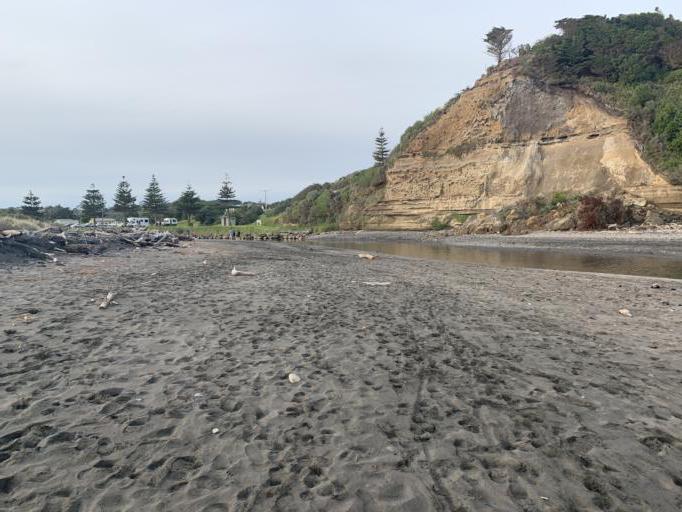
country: NZ
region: Taranaki
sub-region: South Taranaki District
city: Hawera
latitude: -39.5671
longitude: 174.0600
